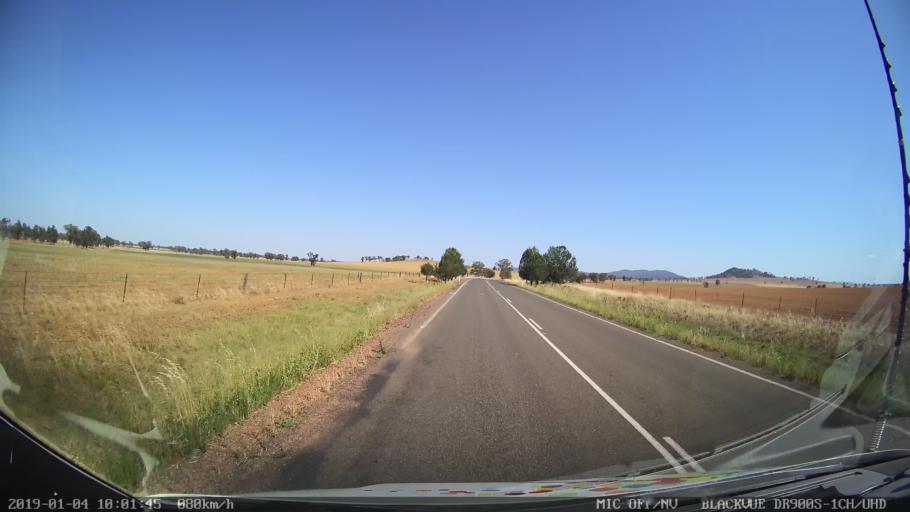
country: AU
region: New South Wales
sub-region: Cabonne
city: Canowindra
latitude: -33.4844
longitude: 148.3680
